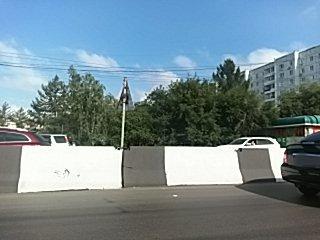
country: RU
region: Krasnoyarskiy
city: Solnechnyy
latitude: 56.0437
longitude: 92.9430
